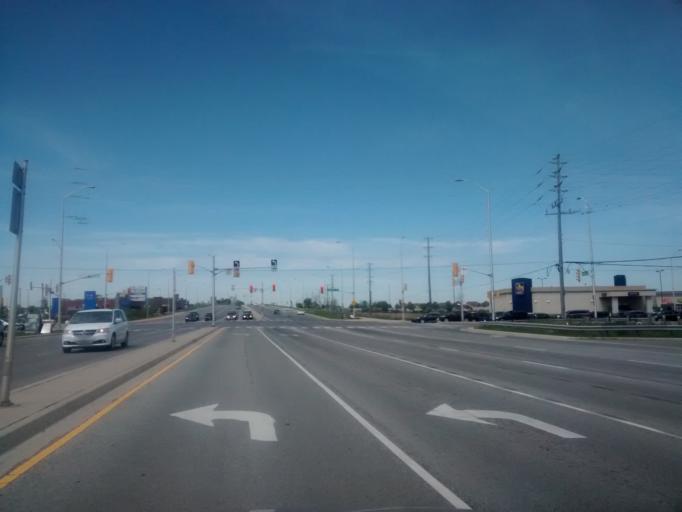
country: CA
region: Ontario
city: Burlington
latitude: 43.4059
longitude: -79.8087
